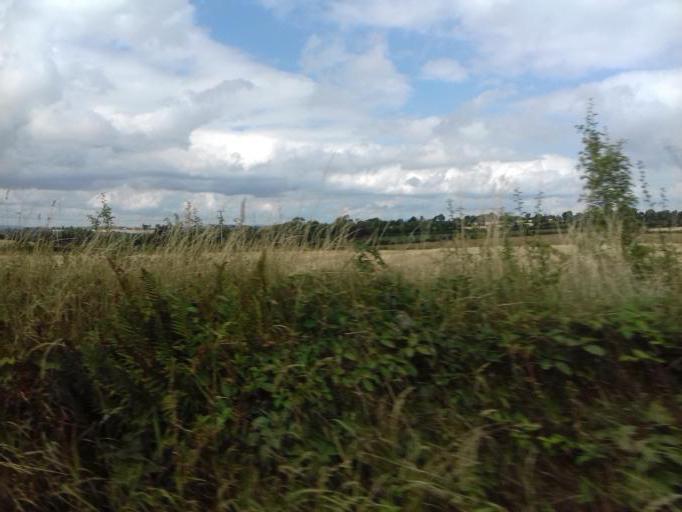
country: IE
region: Leinster
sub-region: Loch Garman
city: Ballinroad
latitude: 52.4889
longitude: -6.4577
